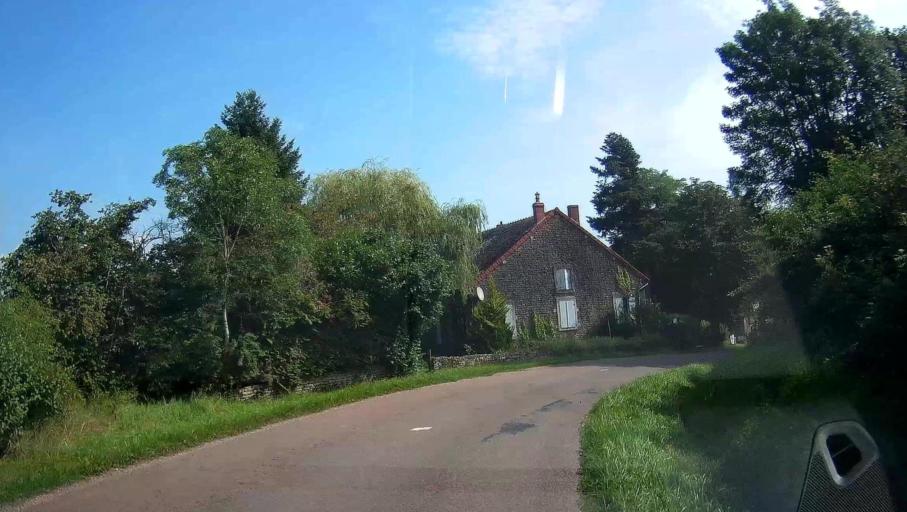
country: FR
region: Bourgogne
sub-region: Departement de la Cote-d'Or
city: Nolay
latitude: 46.9118
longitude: 4.6314
